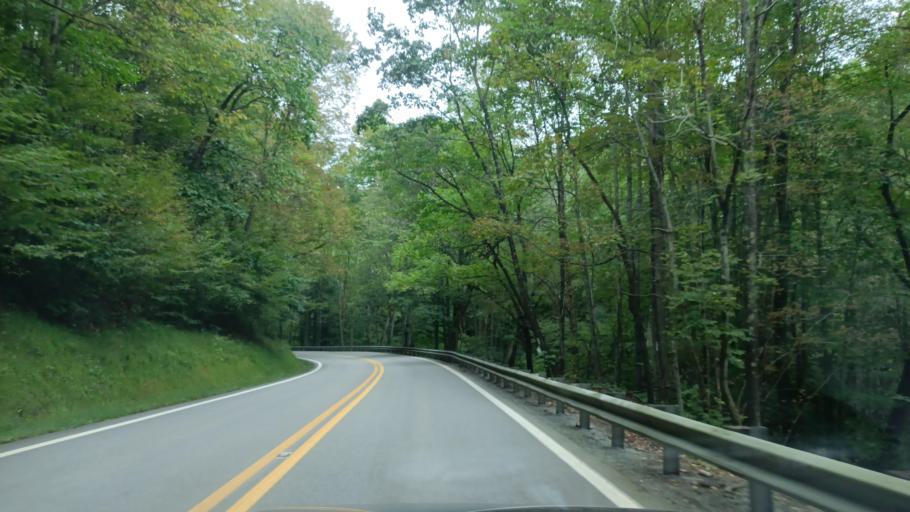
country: US
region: West Virginia
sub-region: Taylor County
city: Grafton
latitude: 39.3400
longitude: -79.9336
